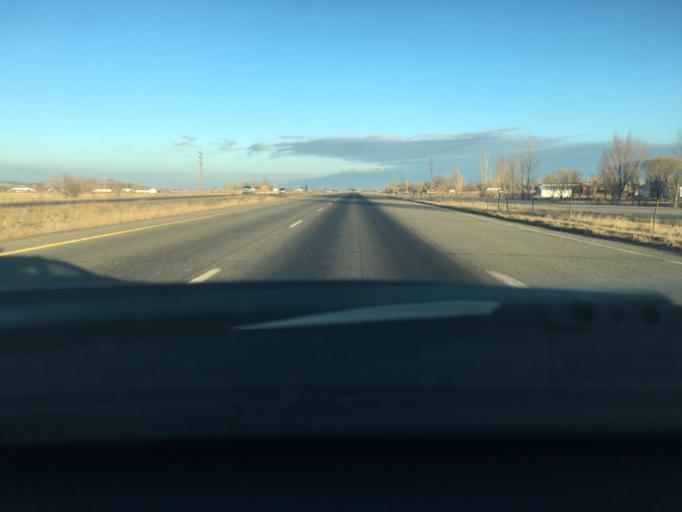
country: US
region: Colorado
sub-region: Montrose County
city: Olathe
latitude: 38.5482
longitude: -107.9469
